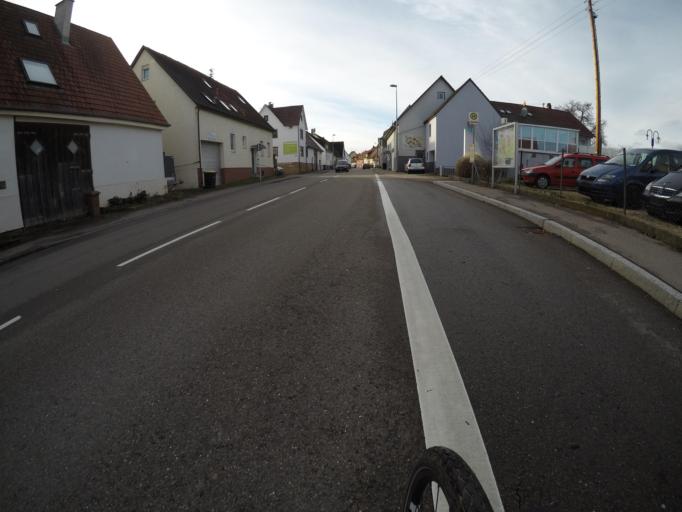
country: DE
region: Baden-Wuerttemberg
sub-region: Regierungsbezirk Stuttgart
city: Oberboihingen
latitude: 48.6305
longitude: 9.3905
